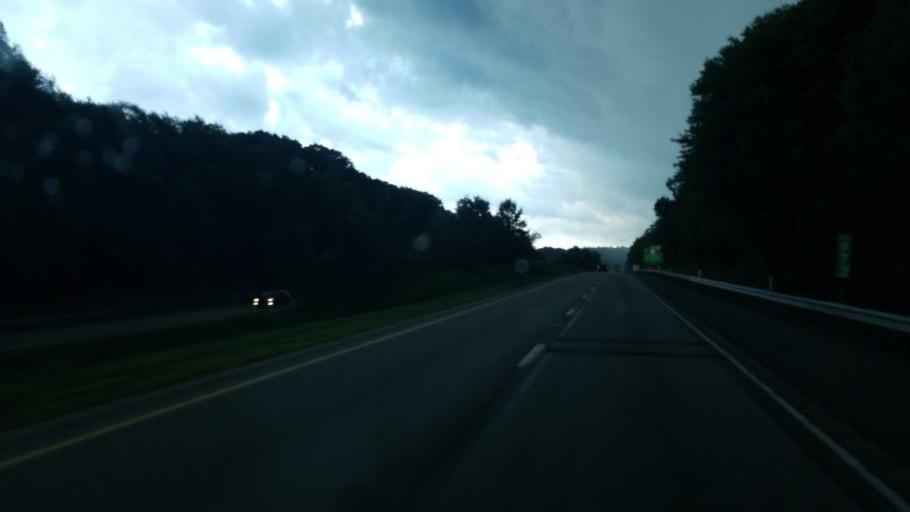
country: US
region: Pennsylvania
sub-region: Butler County
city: Prospect
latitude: 40.9377
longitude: -80.1346
